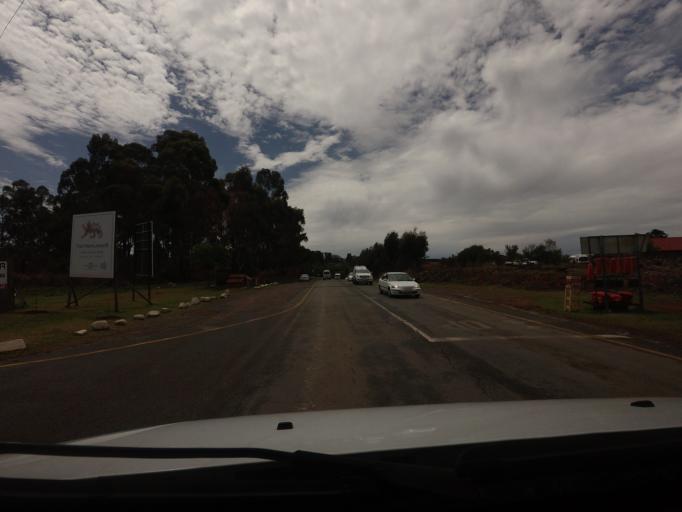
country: ZA
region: Mpumalanga
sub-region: Nkangala District Municipality
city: Belfast
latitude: -25.4230
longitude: 30.1004
